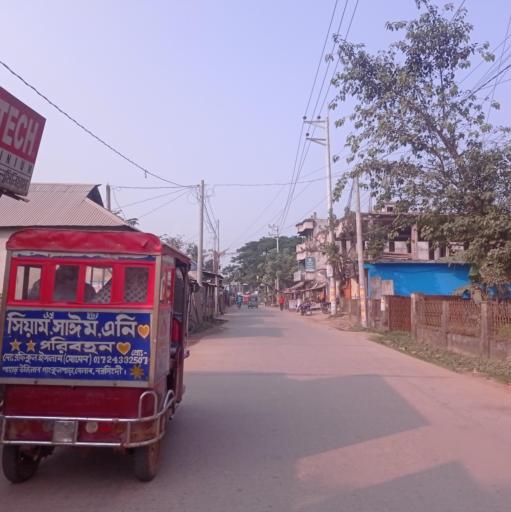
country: BD
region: Dhaka
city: Bhairab Bazar
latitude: 24.1023
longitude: 90.8524
